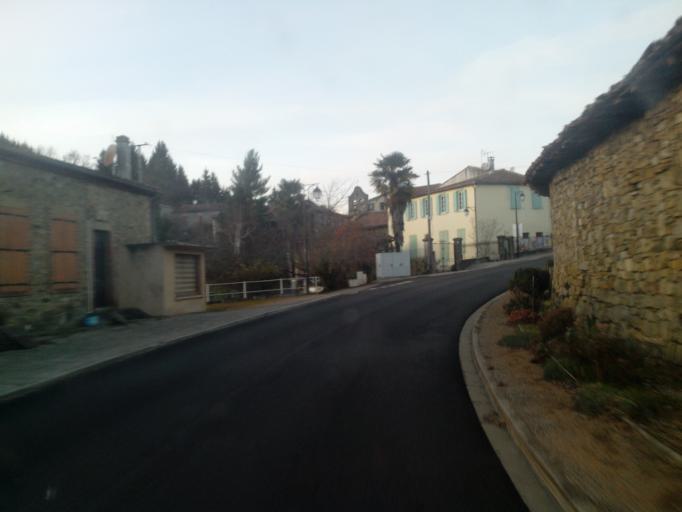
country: FR
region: Midi-Pyrenees
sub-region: Departement de l'Ariege
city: Lavelanet
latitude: 42.9161
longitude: 1.7582
